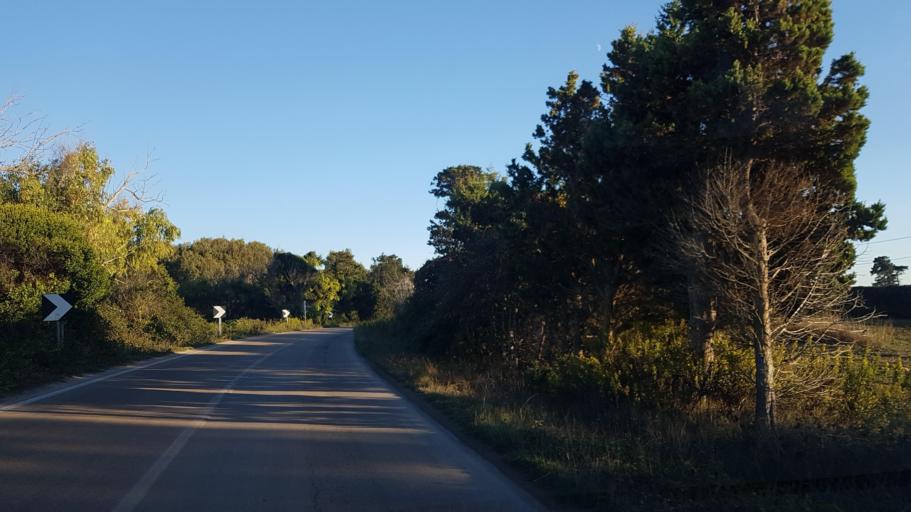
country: IT
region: Apulia
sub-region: Provincia di Lecce
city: Giorgilorio
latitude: 40.4466
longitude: 18.2299
